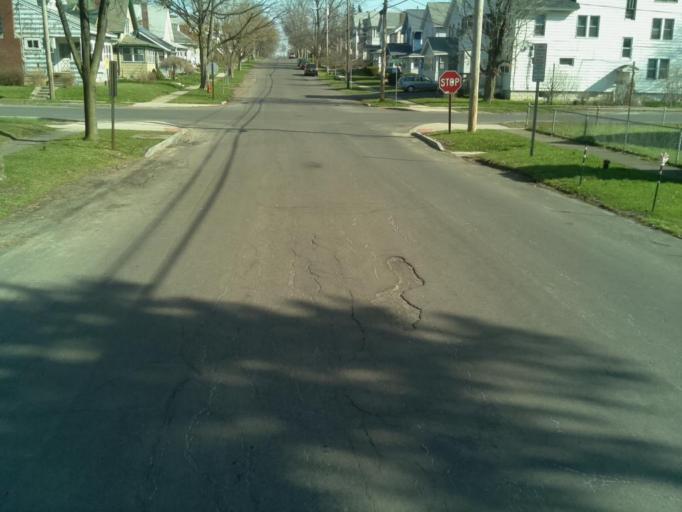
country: US
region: New York
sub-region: Onondaga County
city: Lyncourt
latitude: 43.0585
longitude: -76.1091
